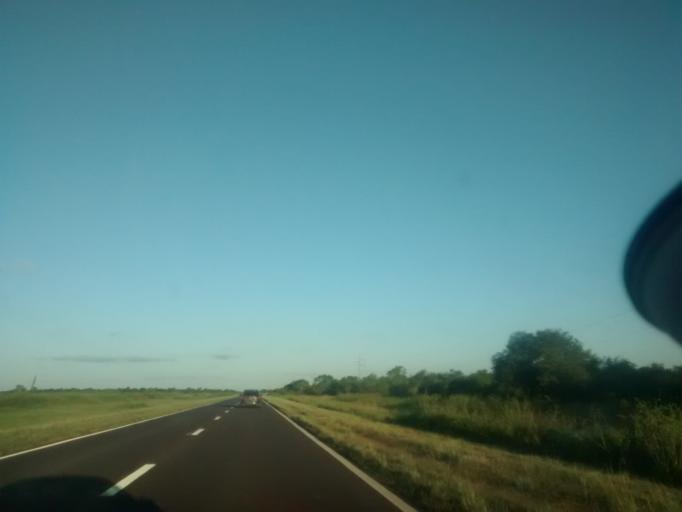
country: AR
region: Chaco
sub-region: Departamento de Presidencia de la Plaza
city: Presidencia de la Plaza
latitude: -27.0213
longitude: -59.8094
